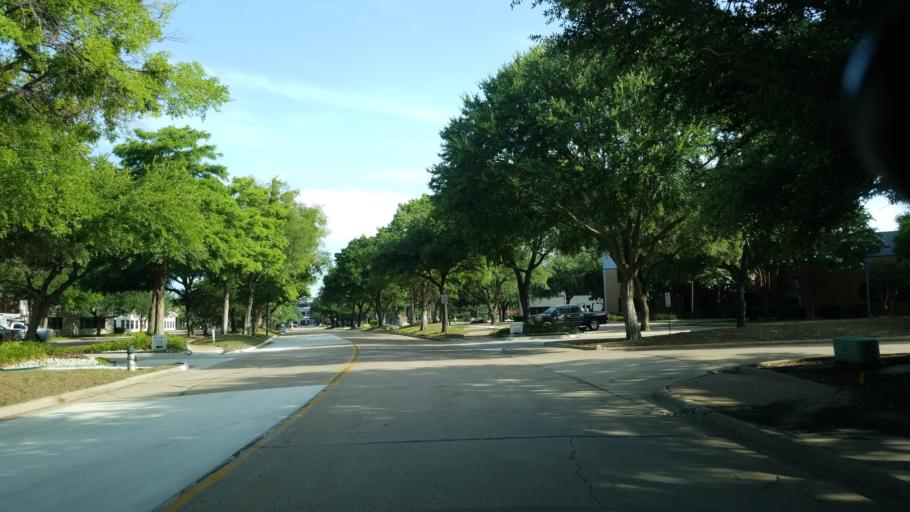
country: US
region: Texas
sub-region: Dallas County
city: Coppell
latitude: 32.9222
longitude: -97.0131
